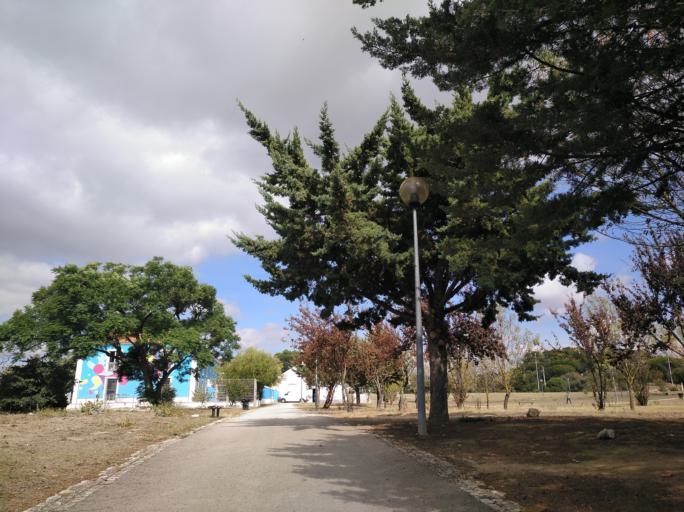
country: PT
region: Lisbon
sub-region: Lisbon
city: Lisbon
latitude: 38.7450
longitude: -9.1244
